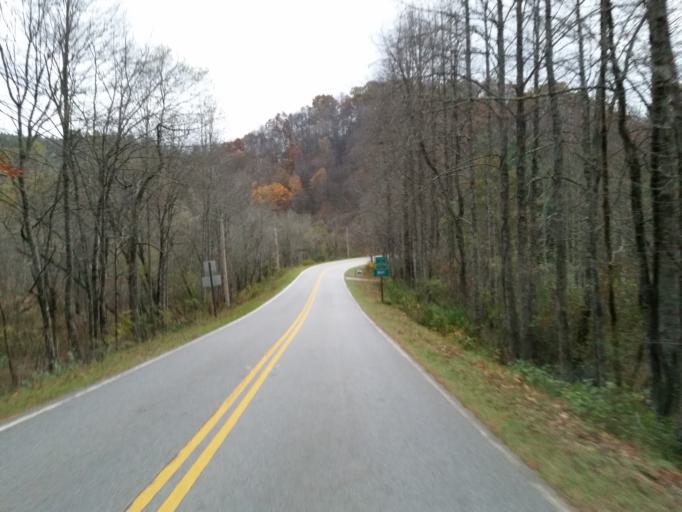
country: US
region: Georgia
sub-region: Union County
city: Blairsville
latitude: 34.7322
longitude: -84.0807
